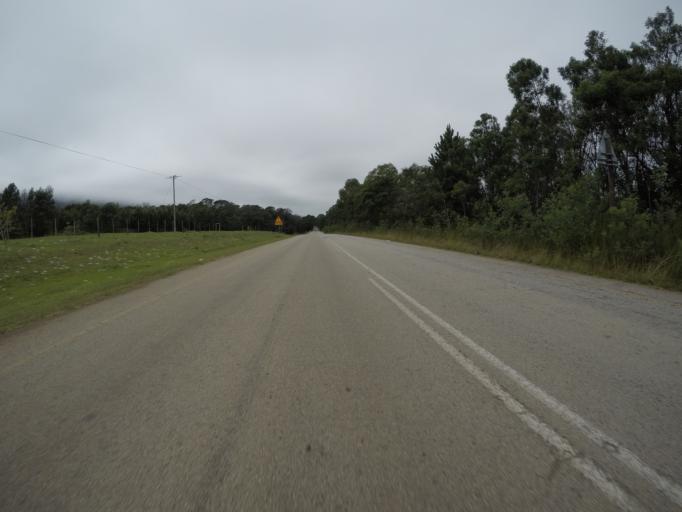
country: ZA
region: Eastern Cape
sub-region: Cacadu District Municipality
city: Kareedouw
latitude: -33.9976
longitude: 24.1662
